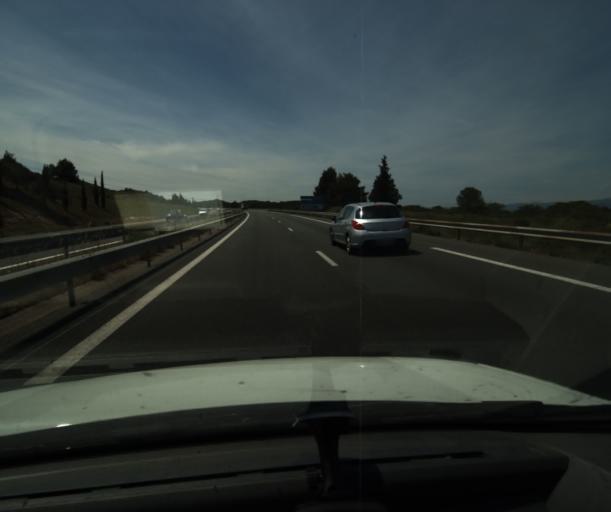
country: FR
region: Languedoc-Roussillon
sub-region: Departement de l'Aude
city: Fabrezan
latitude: 43.1740
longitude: 2.6678
